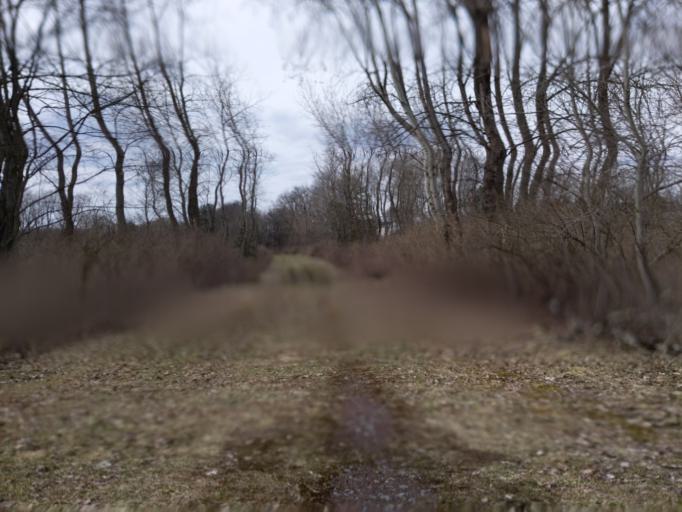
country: US
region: New York
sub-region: Tompkins County
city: Dryden
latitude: 42.4930
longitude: -76.3062
